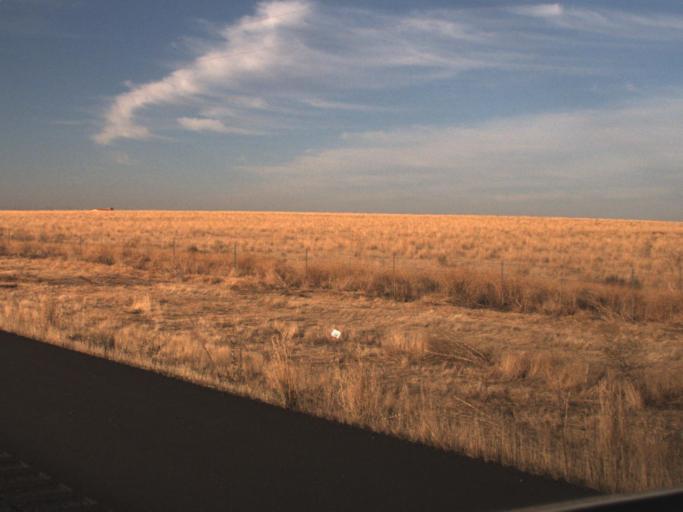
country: US
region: Washington
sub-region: Franklin County
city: Connell
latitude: 46.7260
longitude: -118.8305
